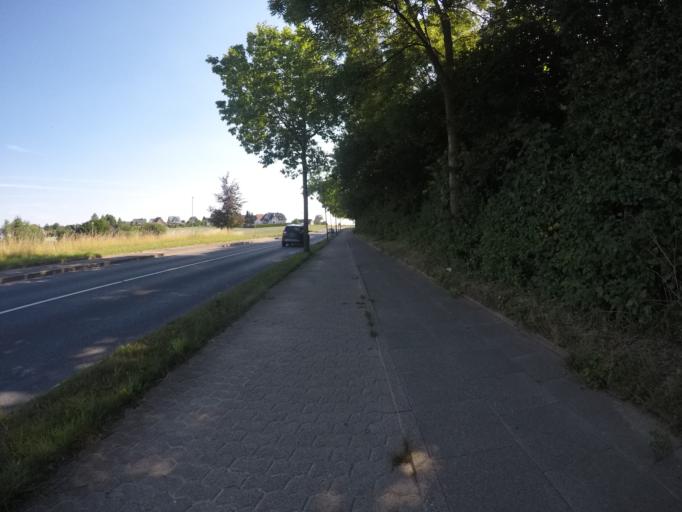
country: DE
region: North Rhine-Westphalia
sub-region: Regierungsbezirk Detmold
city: Herford
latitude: 52.1493
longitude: 8.6590
